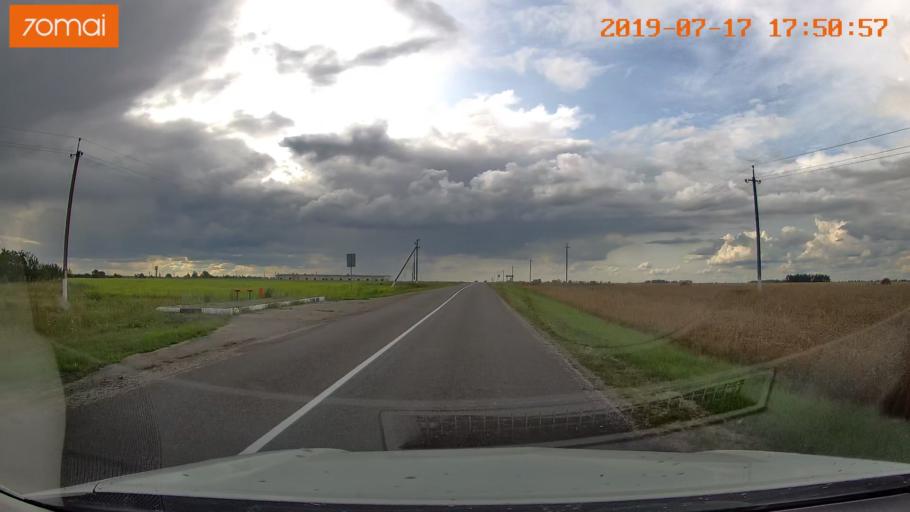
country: BY
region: Mogilev
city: Hlusha
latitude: 53.1465
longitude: 28.7949
